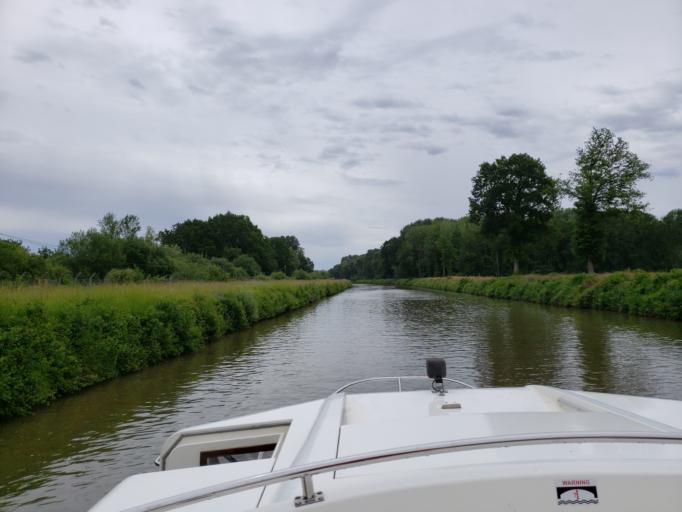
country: FR
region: Bourgogne
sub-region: Departement de l'Yonne
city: Appoigny
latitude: 47.9032
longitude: 3.5346
